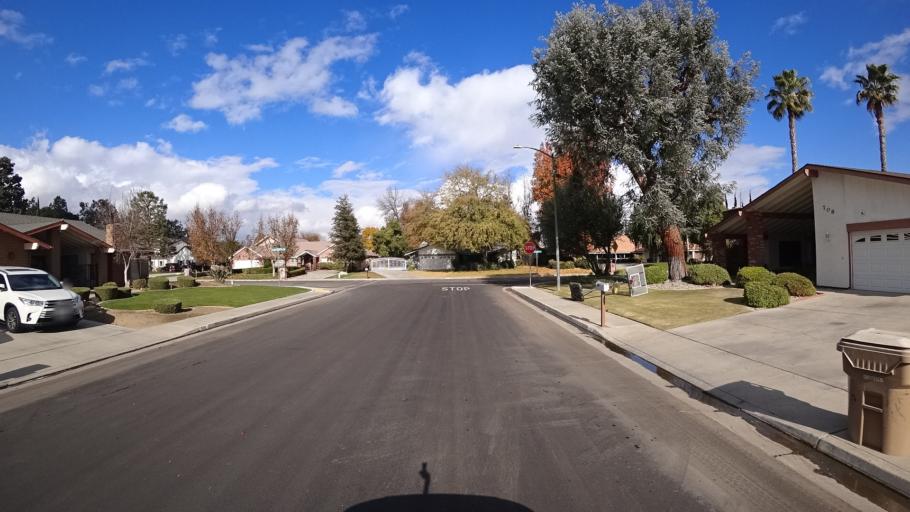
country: US
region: California
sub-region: Kern County
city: Greenacres
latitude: 35.3595
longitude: -119.0823
